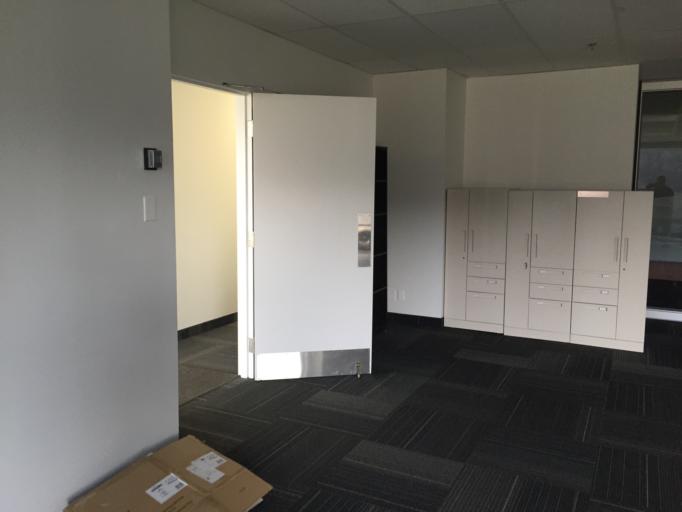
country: CA
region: Ontario
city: Thorold
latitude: 43.1540
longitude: -79.1613
